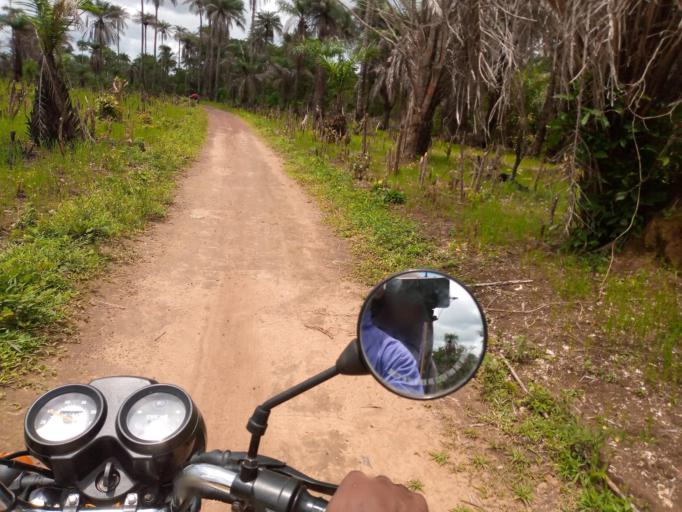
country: SL
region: Northern Province
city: Mange
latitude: 8.9918
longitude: -12.7777
